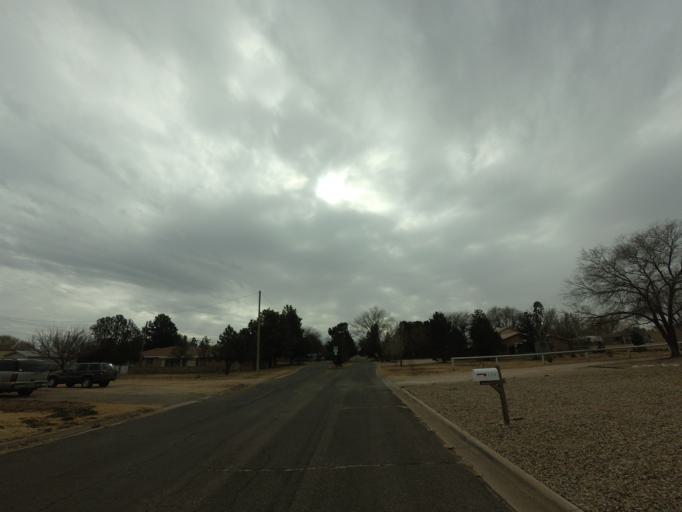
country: US
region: New Mexico
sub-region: Curry County
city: Clovis
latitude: 34.3809
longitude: -103.2008
